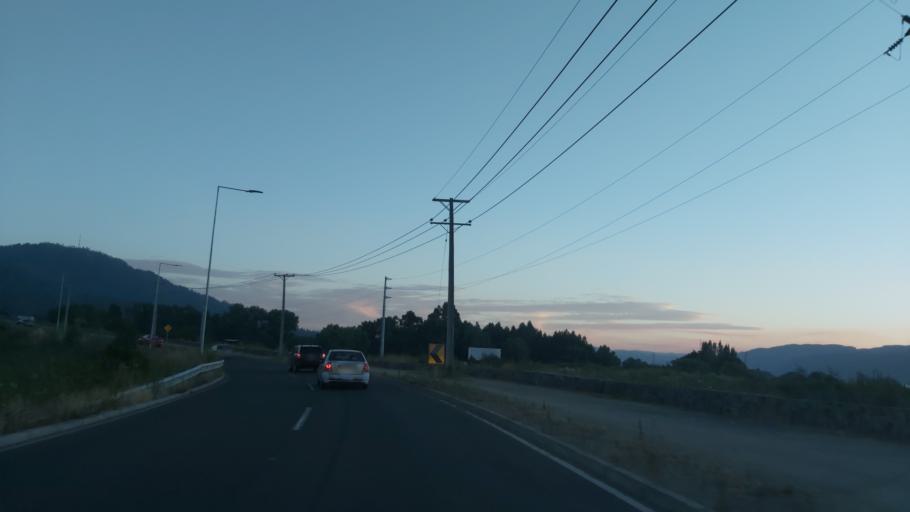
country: CL
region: Biobio
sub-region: Provincia de Concepcion
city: Chiguayante
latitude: -36.8938
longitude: -73.0364
